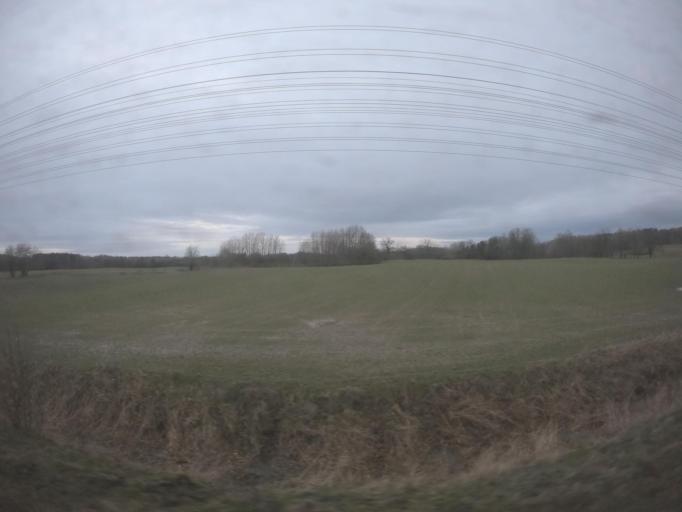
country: PL
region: West Pomeranian Voivodeship
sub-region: Powiat szczecinecki
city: Borne Sulinowo
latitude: 53.6572
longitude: 16.5443
